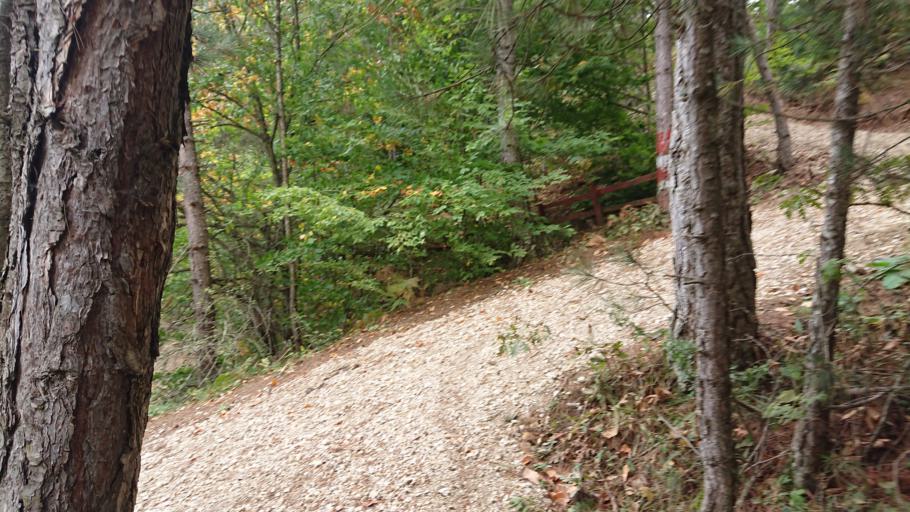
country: TR
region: Bilecik
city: Pazaryeri
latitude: 40.0138
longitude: 29.7953
